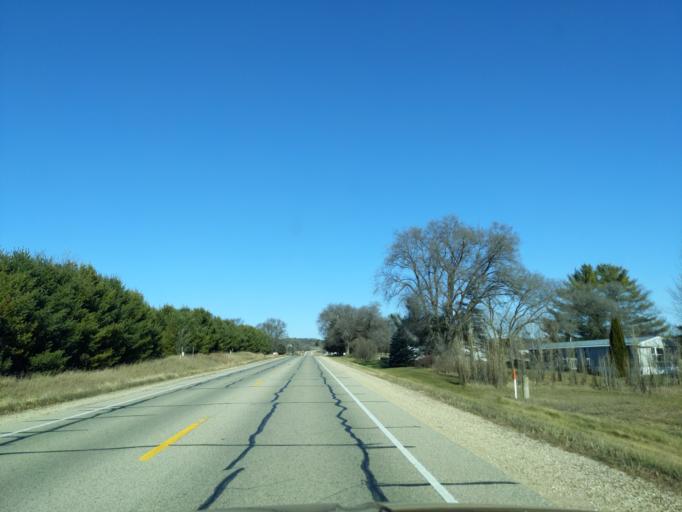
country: US
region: Wisconsin
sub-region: Waushara County
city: Wautoma
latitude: 44.0950
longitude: -89.2914
